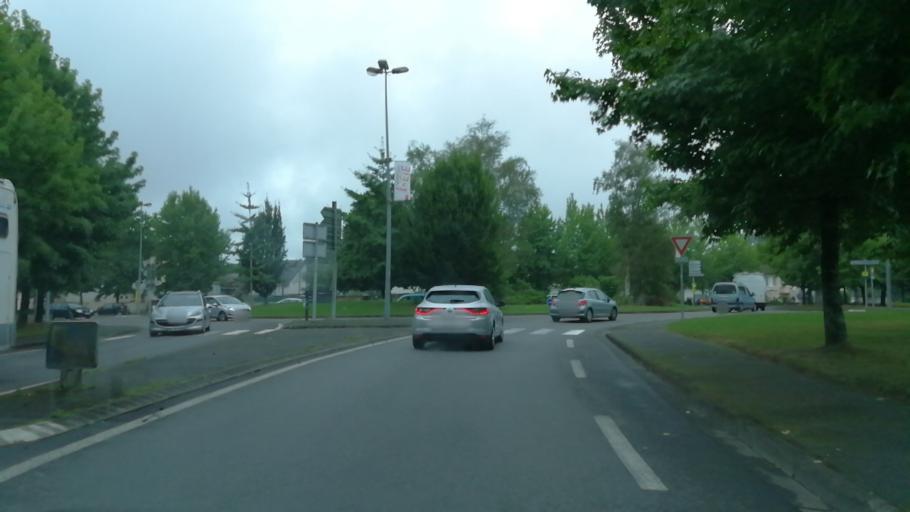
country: FR
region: Aquitaine
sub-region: Departement des Pyrenees-Atlantiques
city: Oloron-Sainte-Marie
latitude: 43.1876
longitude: -0.6250
